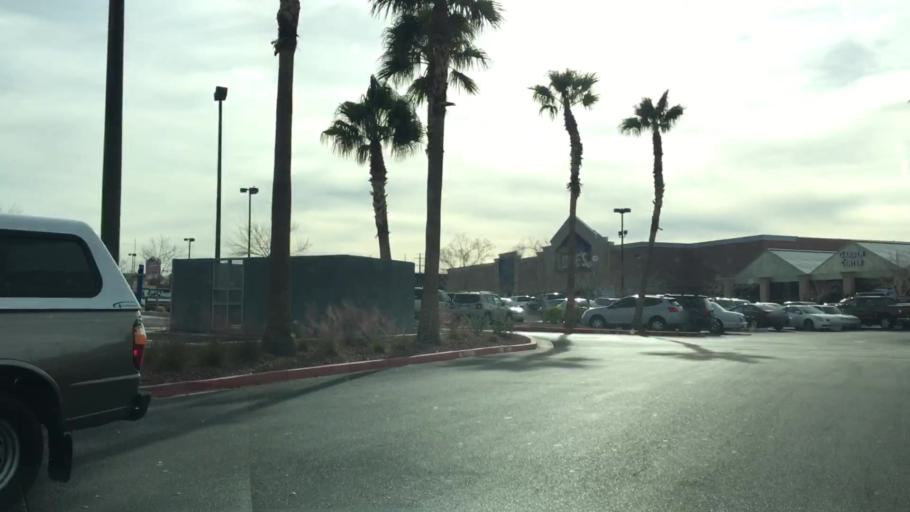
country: US
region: Nevada
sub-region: Clark County
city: Whitney
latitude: 36.0088
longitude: -115.1166
